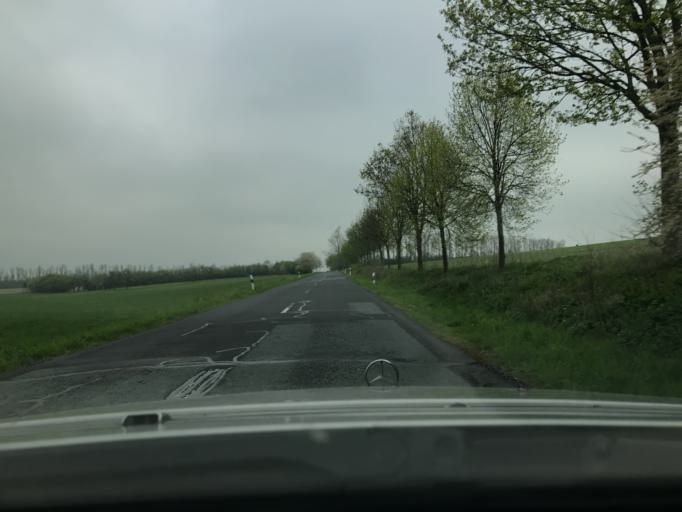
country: DE
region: Thuringia
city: Kefferhausen
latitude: 51.3276
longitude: 10.2705
